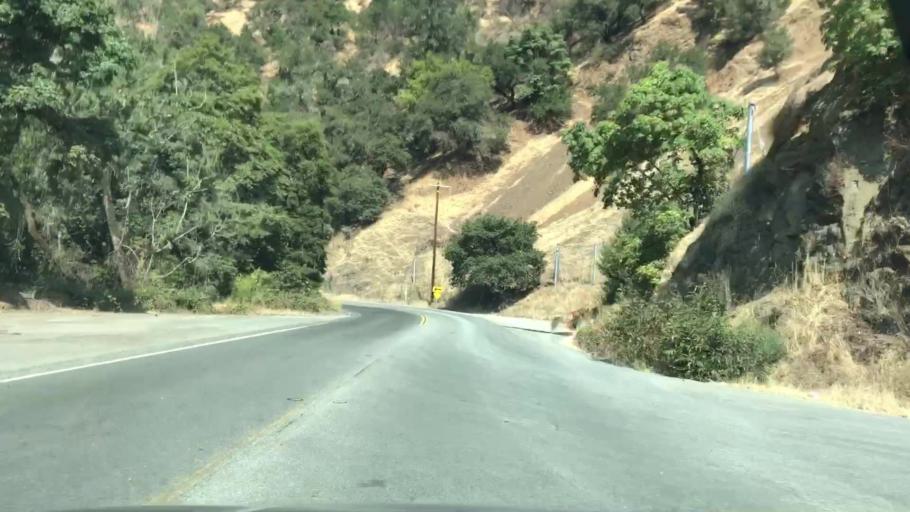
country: US
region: California
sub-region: Napa County
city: Calistoga
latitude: 38.5543
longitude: -122.6565
